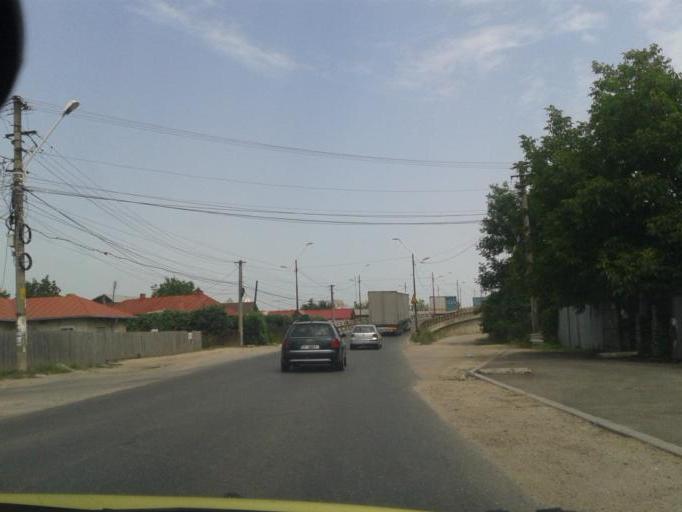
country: RO
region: Dambovita
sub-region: Oras Gaesti
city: Gaesti
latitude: 44.7100
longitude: 25.3093
